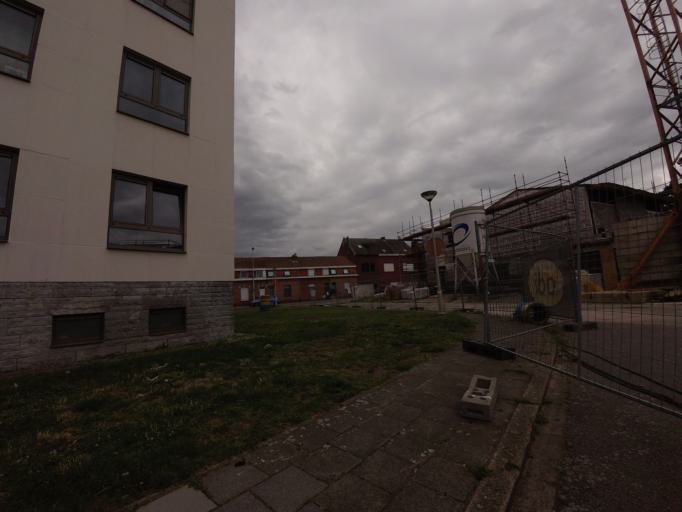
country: BE
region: Flanders
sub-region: Provincie Antwerpen
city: Duffel
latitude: 51.0951
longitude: 4.5146
